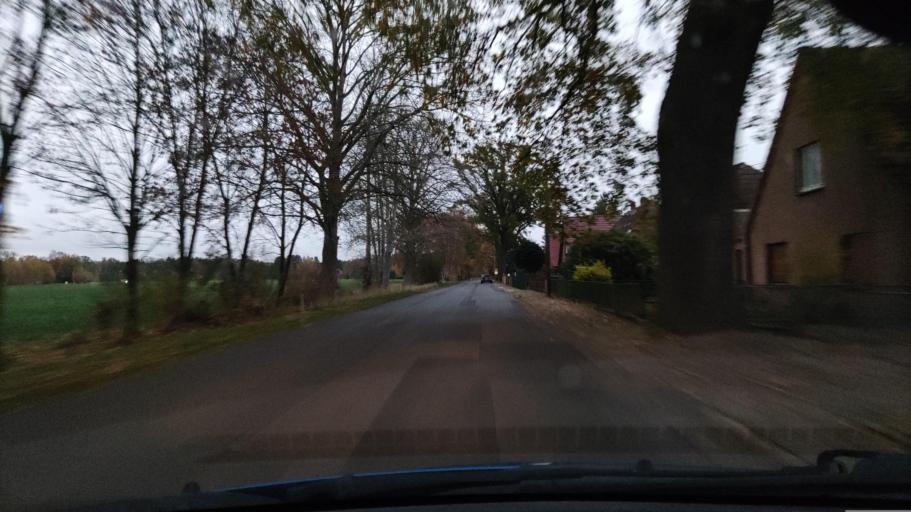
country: DE
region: Mecklenburg-Vorpommern
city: Domitz
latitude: 53.1770
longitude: 11.2401
